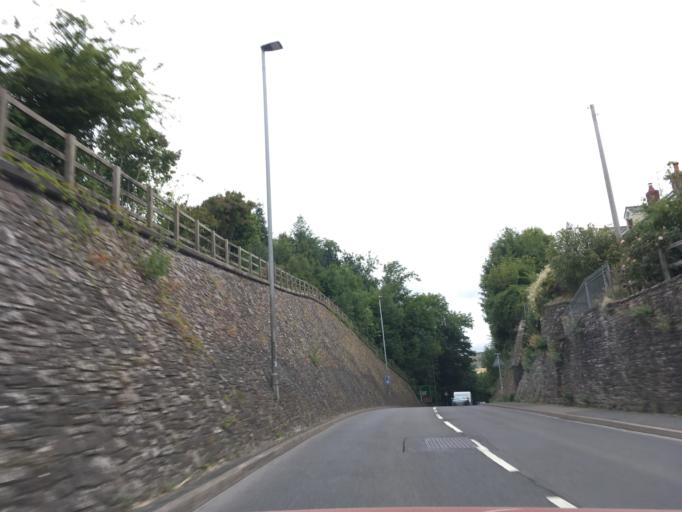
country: GB
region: Wales
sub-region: Blaenau Gwent
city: Brynmawr
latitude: 51.8908
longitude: -3.2392
